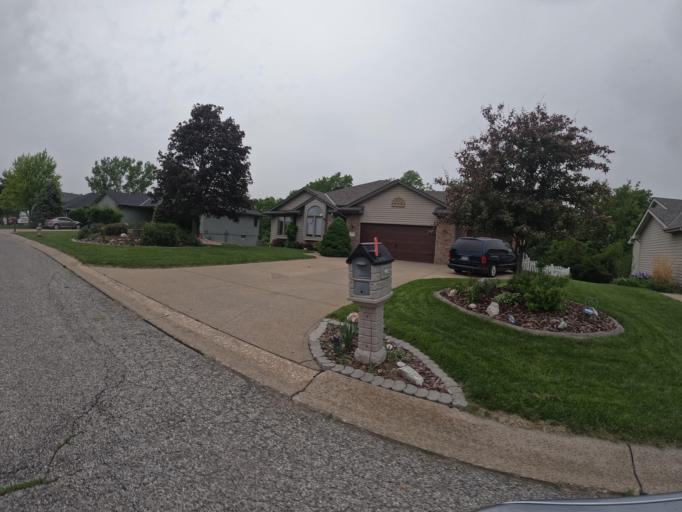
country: US
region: Nebraska
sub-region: Sarpy County
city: Offutt Air Force Base
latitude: 41.0502
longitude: -95.9734
